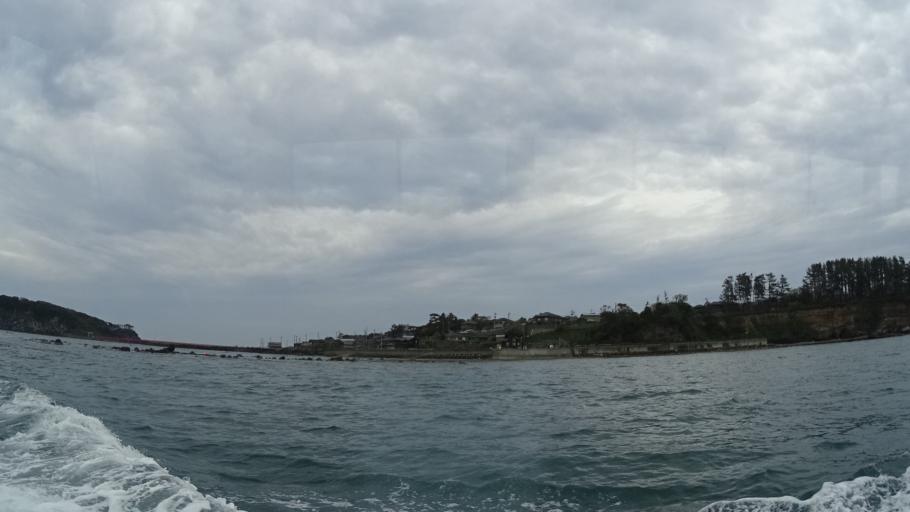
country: JP
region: Fukui
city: Mikuni
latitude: 36.2444
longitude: 136.1239
